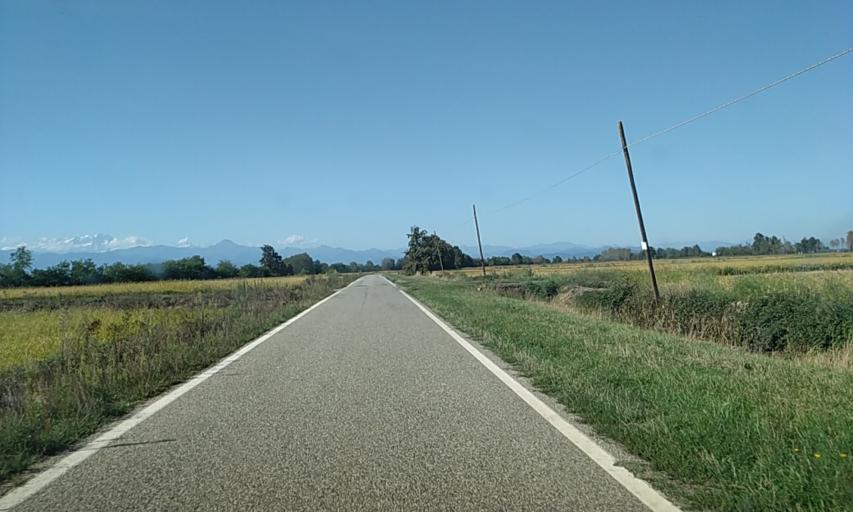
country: IT
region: Piedmont
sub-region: Provincia di Vercelli
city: San Giacomo Vercellese
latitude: 45.4814
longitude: 8.3377
